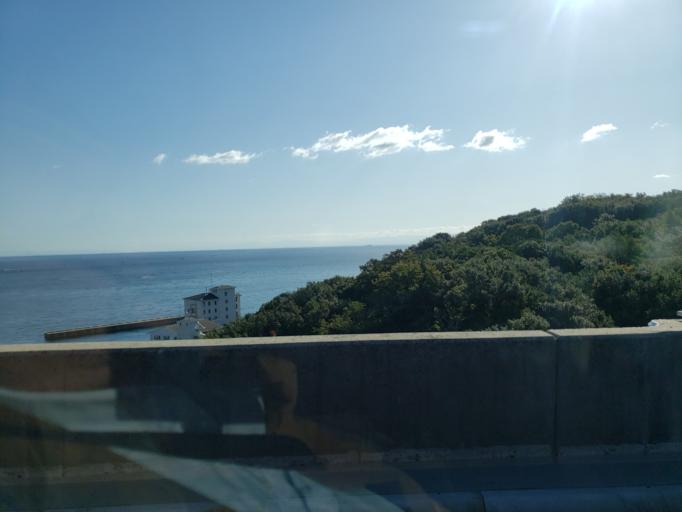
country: JP
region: Hyogo
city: Akashi
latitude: 34.6005
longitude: 135.0075
